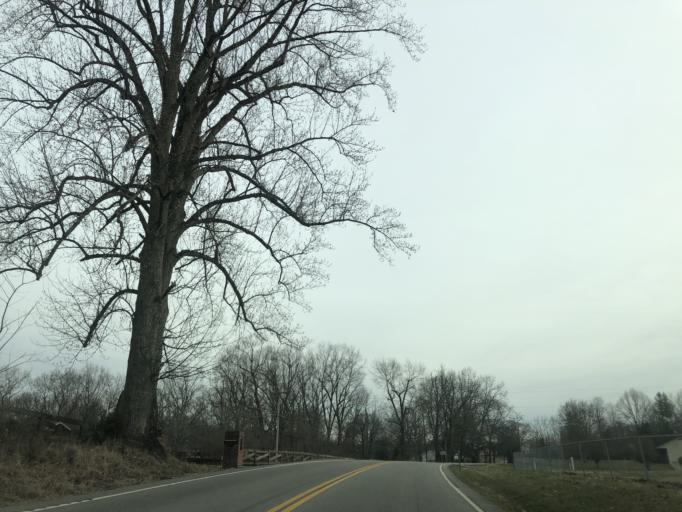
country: US
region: Tennessee
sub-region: Sumner County
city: White House
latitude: 36.5095
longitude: -86.6108
